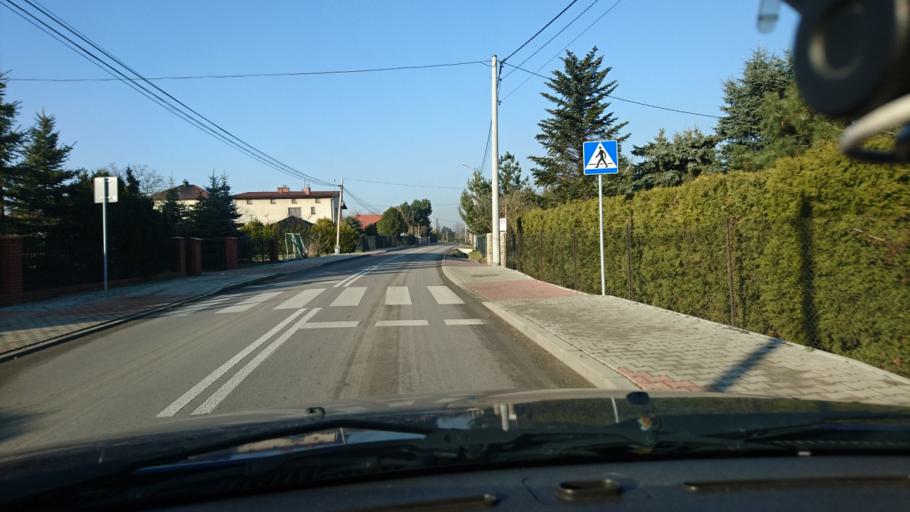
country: PL
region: Silesian Voivodeship
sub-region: Powiat bielski
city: Bestwina
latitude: 49.8935
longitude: 19.0763
